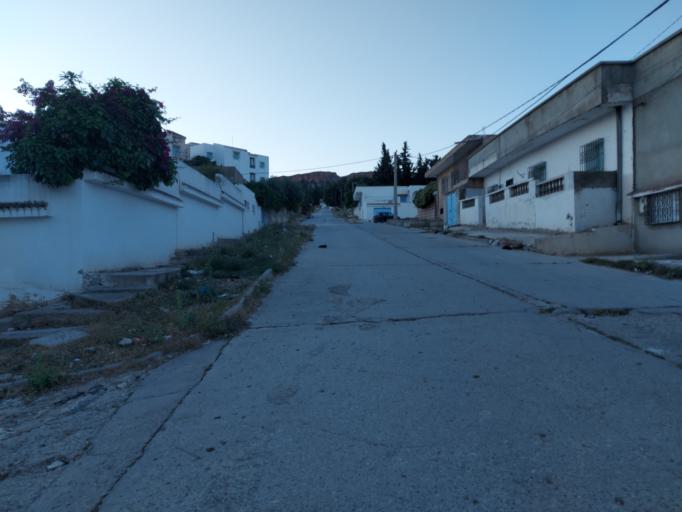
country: TN
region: Kef
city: El Kef
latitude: 36.1813
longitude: 8.7290
